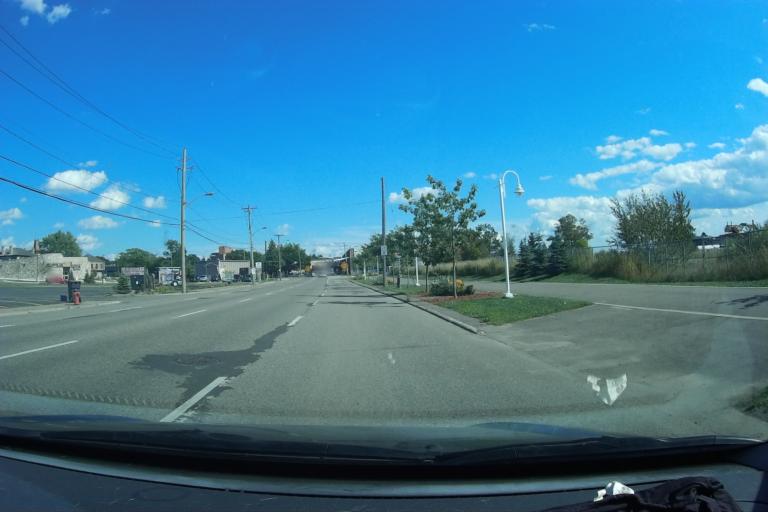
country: CA
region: Ontario
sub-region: Algoma
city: Sault Ste. Marie
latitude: 46.5060
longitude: -84.3268
